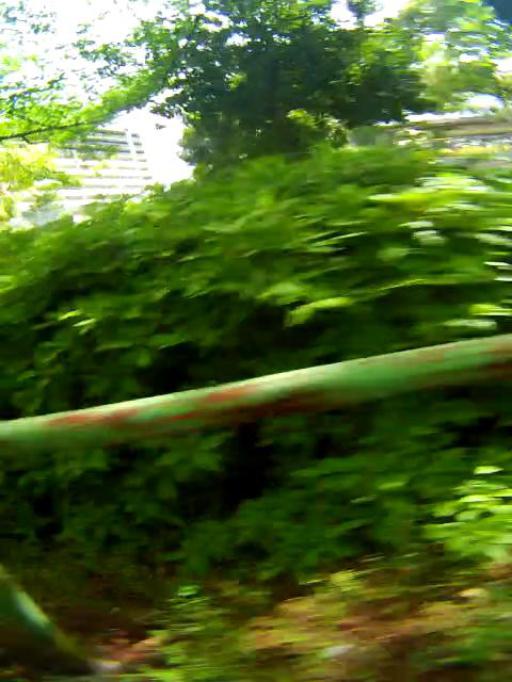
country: JP
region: Osaka
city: Osaka-shi
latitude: 34.7005
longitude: 135.5226
